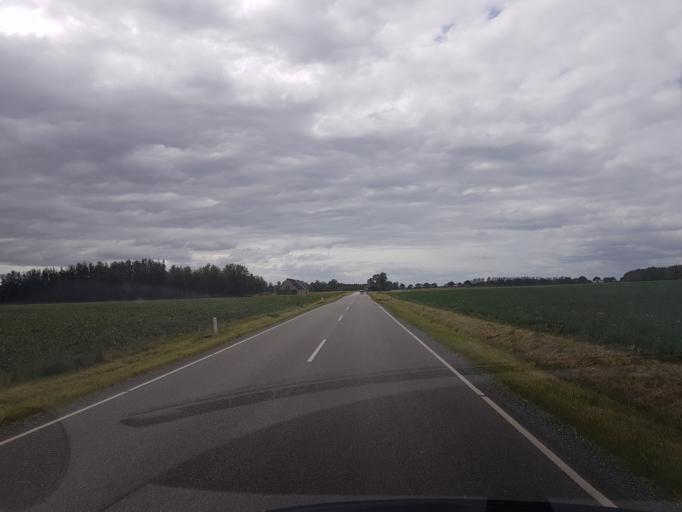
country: DK
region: South Denmark
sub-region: Nordfyns Kommune
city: Bogense
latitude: 55.5675
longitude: 10.1721
